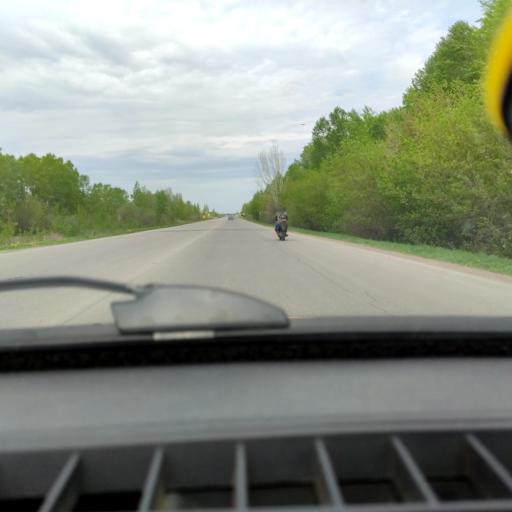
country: RU
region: Samara
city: Tol'yatti
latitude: 53.6960
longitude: 49.4195
